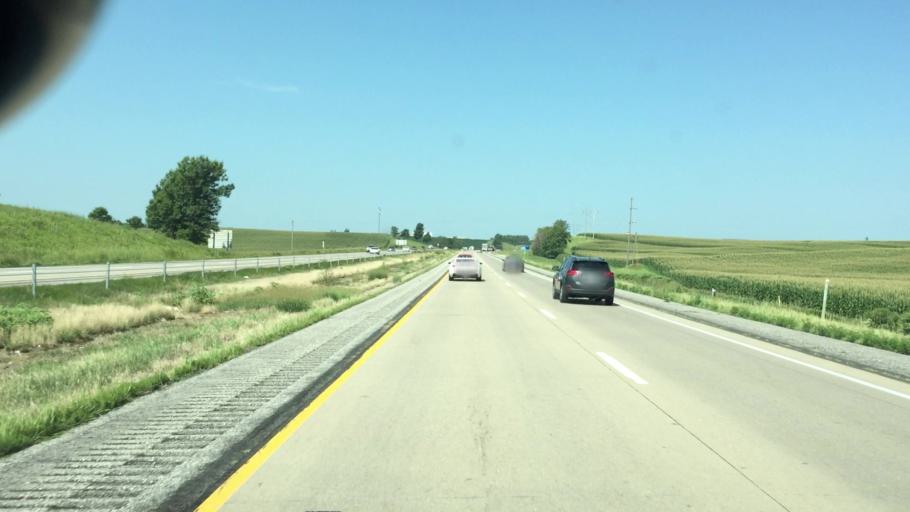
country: US
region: Iowa
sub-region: Iowa County
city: Williamsburg
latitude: 41.6873
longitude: -92.0432
